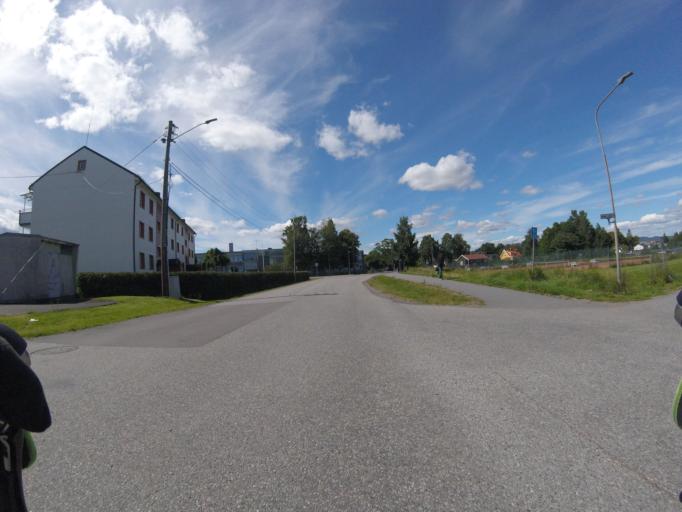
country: NO
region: Akershus
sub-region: Skedsmo
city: Lillestrom
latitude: 59.9507
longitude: 11.0177
